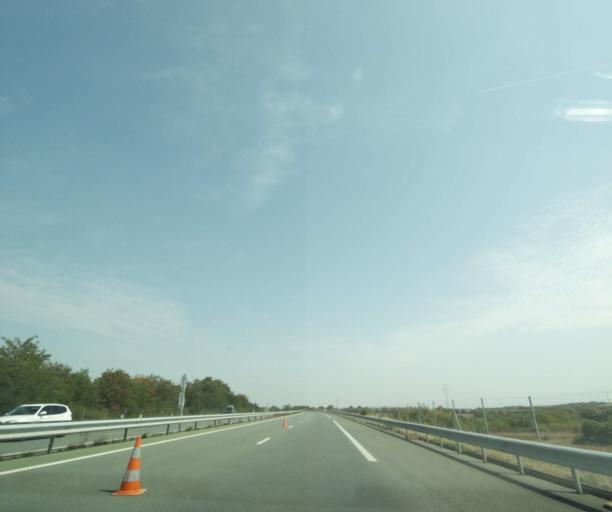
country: FR
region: Pays de la Loire
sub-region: Departement de la Vendee
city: Benet
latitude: 46.4031
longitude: -0.5953
